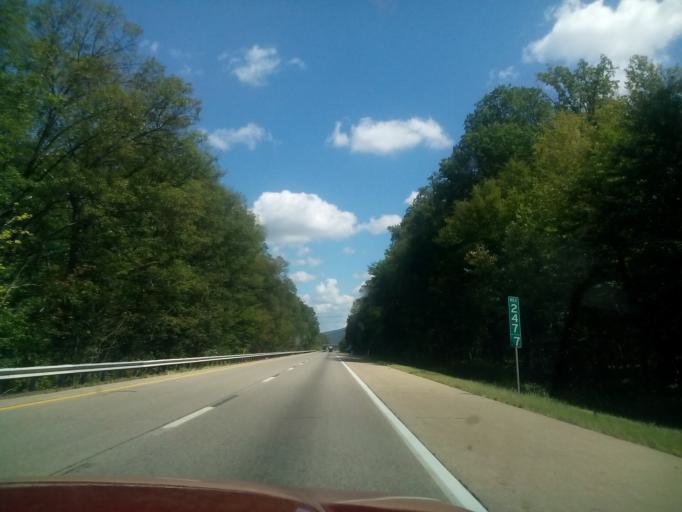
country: US
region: Pennsylvania
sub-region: Luzerne County
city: Nescopeck
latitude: 41.0135
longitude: -76.2160
